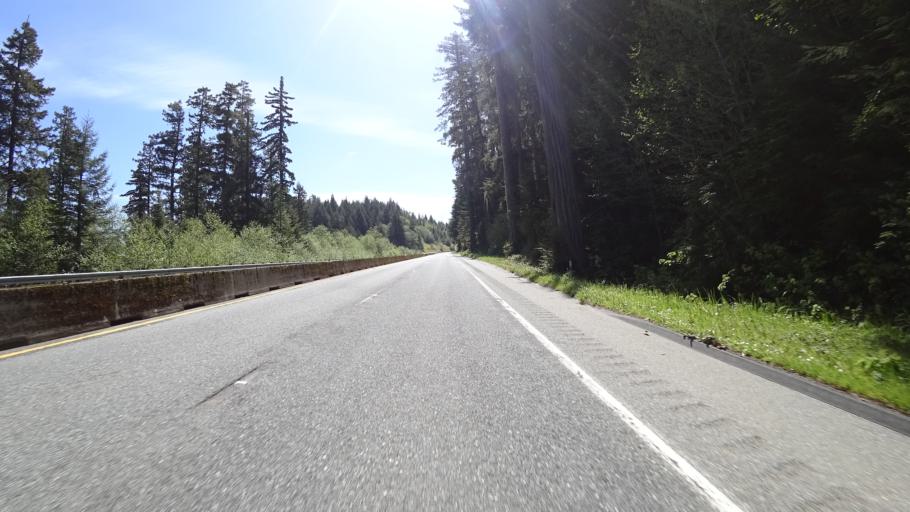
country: US
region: California
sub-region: Humboldt County
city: Westhaven-Moonstone
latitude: 41.4053
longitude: -123.9971
